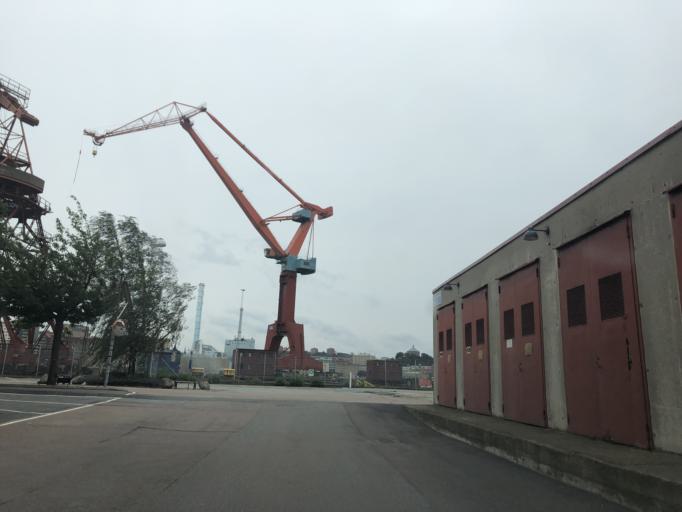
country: SE
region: Vaestra Goetaland
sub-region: Goteborg
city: Goeteborg
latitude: 57.7075
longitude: 11.9479
